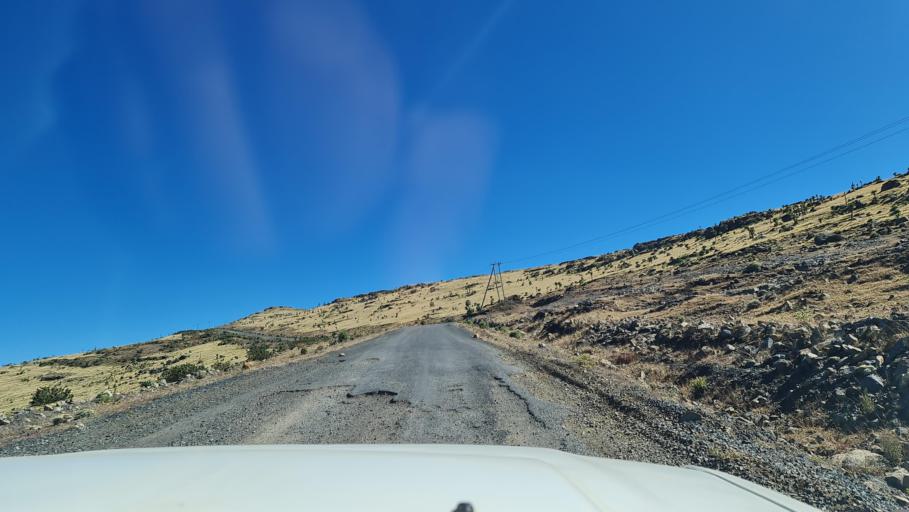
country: ET
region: Amhara
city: Debark'
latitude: 13.1621
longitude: 38.1930
